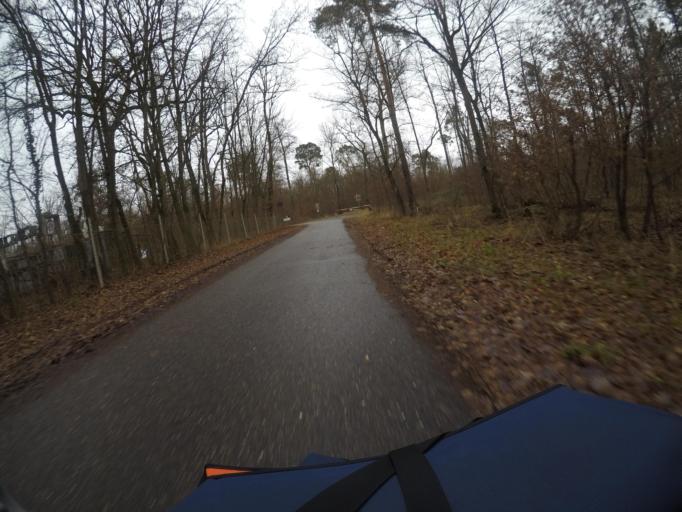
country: DE
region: Baden-Wuerttemberg
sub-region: Karlsruhe Region
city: Philippsburg
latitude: 49.2204
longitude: 8.4782
